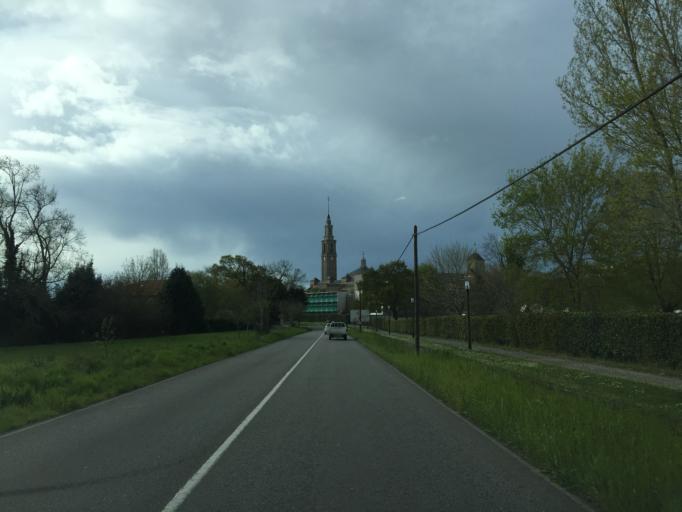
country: ES
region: Asturias
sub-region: Province of Asturias
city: Gijon
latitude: 43.5207
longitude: -5.6105
